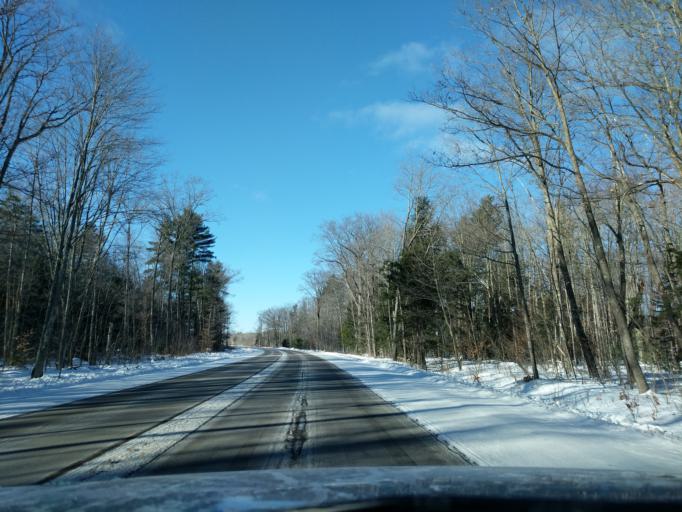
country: US
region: Wisconsin
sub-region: Menominee County
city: Keshena
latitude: 45.1481
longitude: -88.6853
